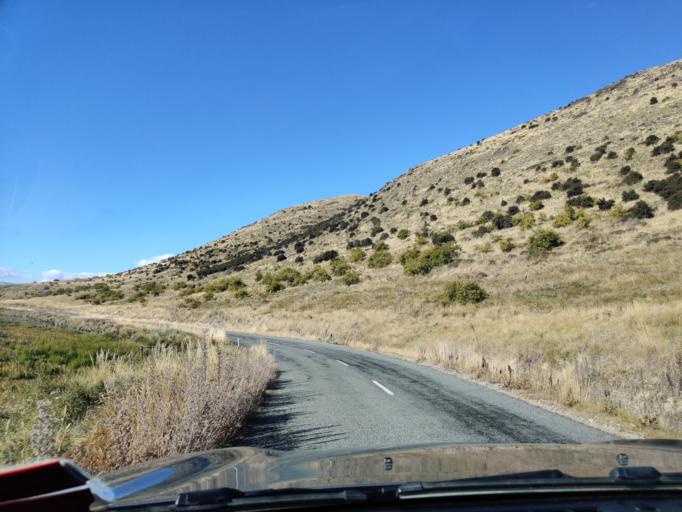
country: NZ
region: Canterbury
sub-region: Timaru District
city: Pleasant Point
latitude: -43.9791
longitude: 170.4622
